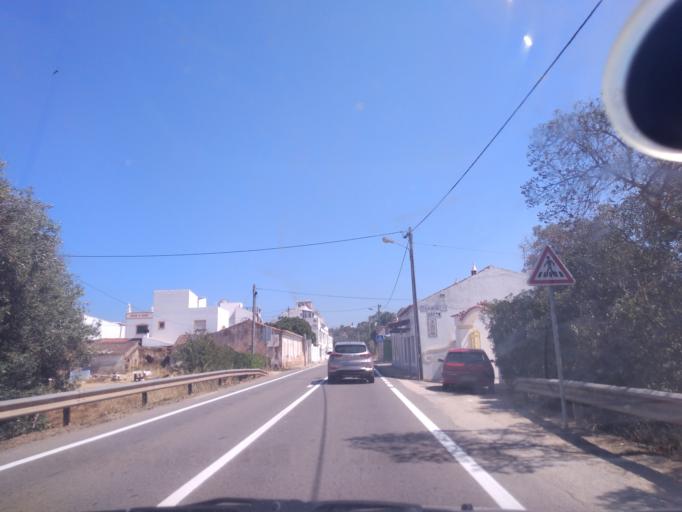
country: PT
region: Faro
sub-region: Lagos
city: Lagos
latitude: 37.1226
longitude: -8.6941
